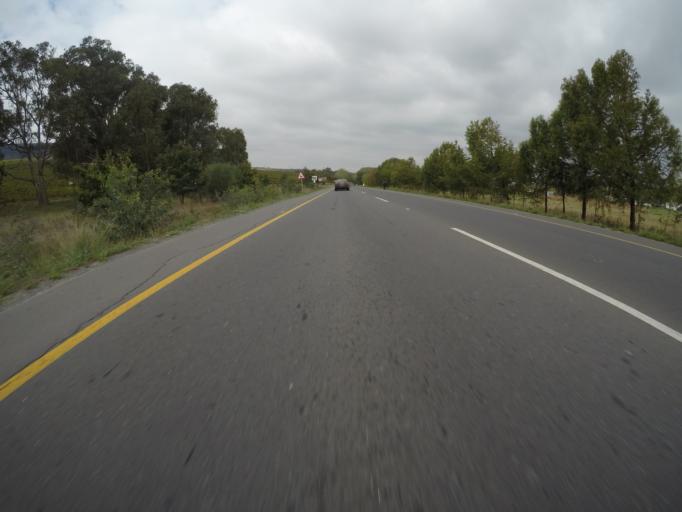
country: ZA
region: Western Cape
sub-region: City of Cape Town
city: Sunset Beach
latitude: -33.8386
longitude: 18.5971
